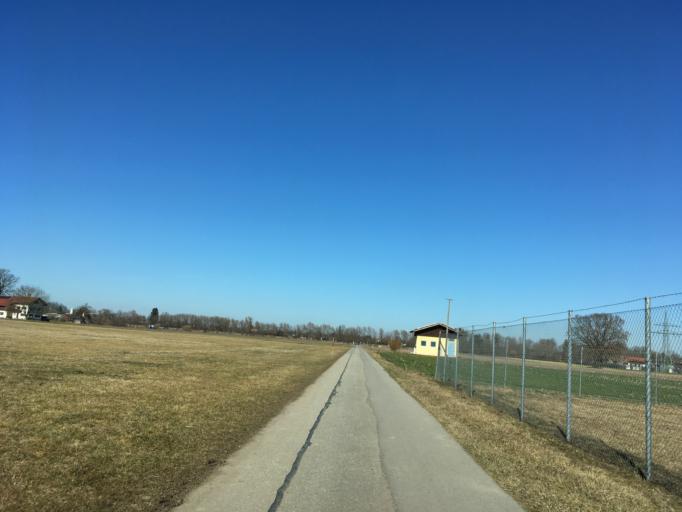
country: DE
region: Bavaria
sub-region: Upper Bavaria
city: Bad Aibling
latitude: 47.8474
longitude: 11.9993
